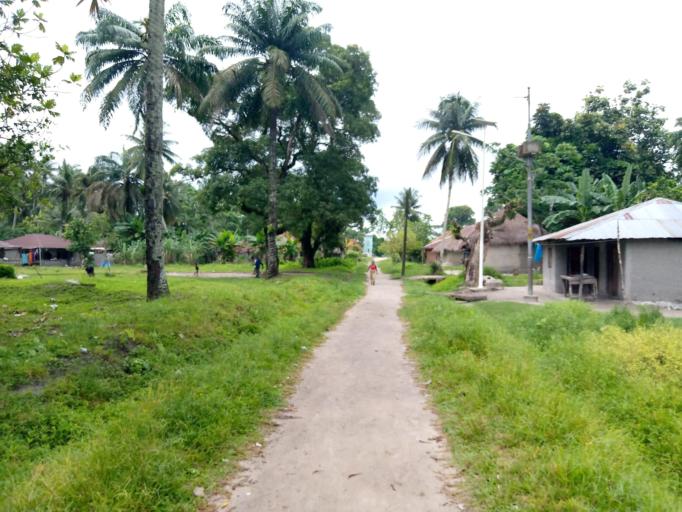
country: SL
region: Southern Province
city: Bonthe
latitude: 7.5310
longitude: -12.5055
